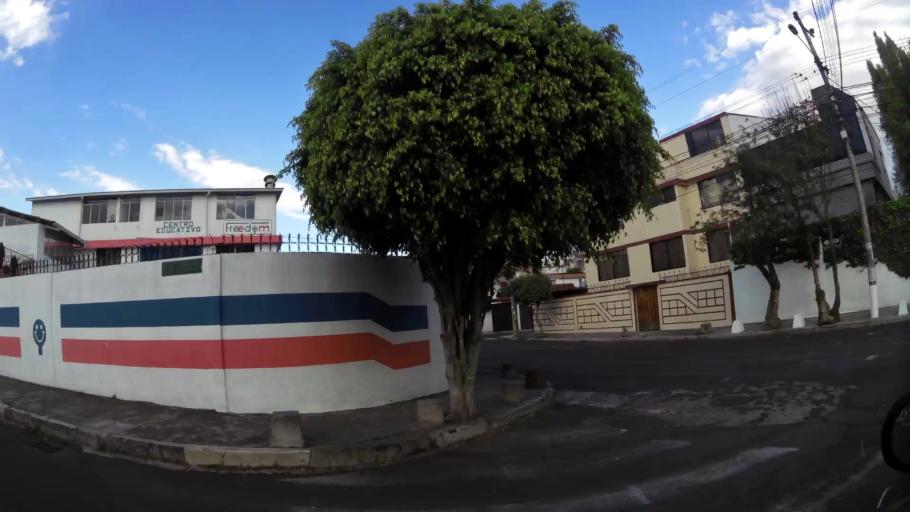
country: EC
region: Pichincha
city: Quito
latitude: -0.1476
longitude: -78.4830
